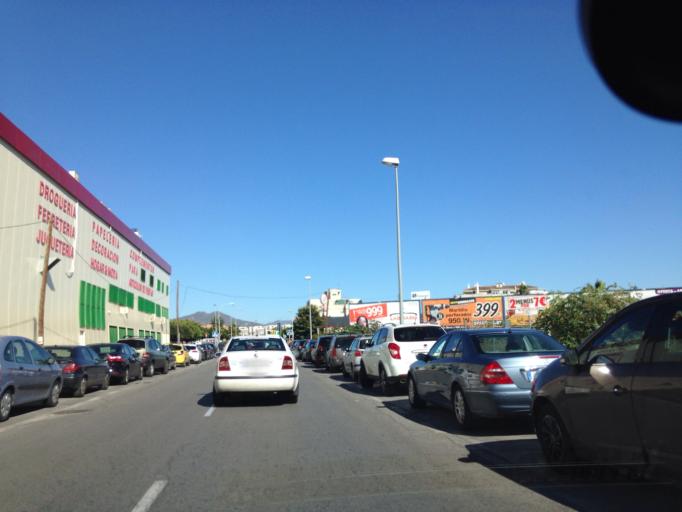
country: ES
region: Andalusia
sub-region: Provincia de Malaga
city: Malaga
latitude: 36.6852
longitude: -4.4576
